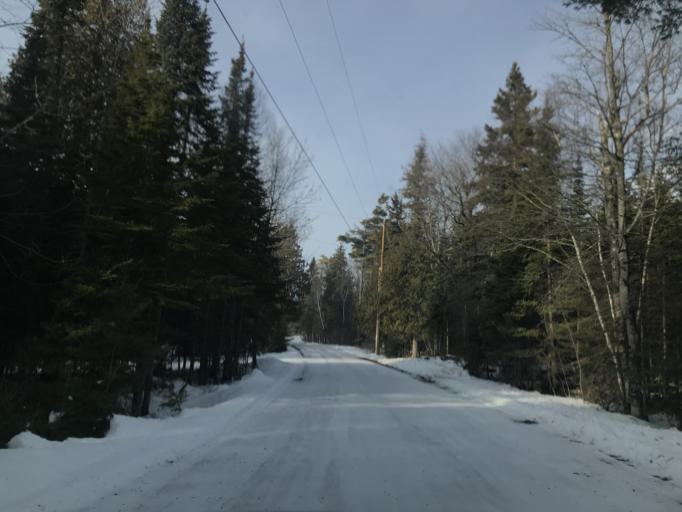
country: US
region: Wisconsin
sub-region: Door County
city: Sturgeon Bay
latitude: 45.1421
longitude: -87.0514
